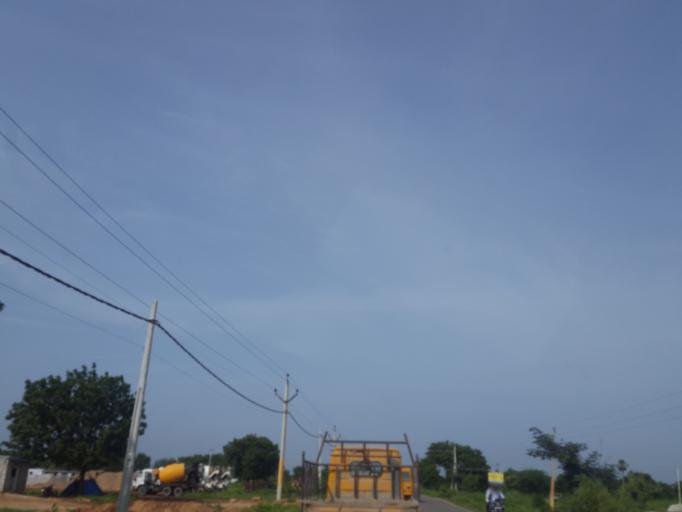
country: IN
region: Telangana
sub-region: Medak
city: Patancheru
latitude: 17.5094
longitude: 78.2171
